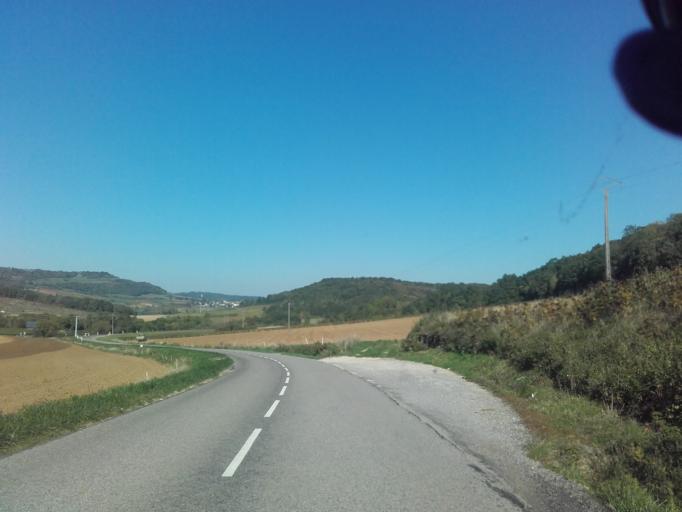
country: FR
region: Bourgogne
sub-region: Departement de la Cote-d'Or
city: Meursault
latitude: 47.0111
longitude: 4.7160
